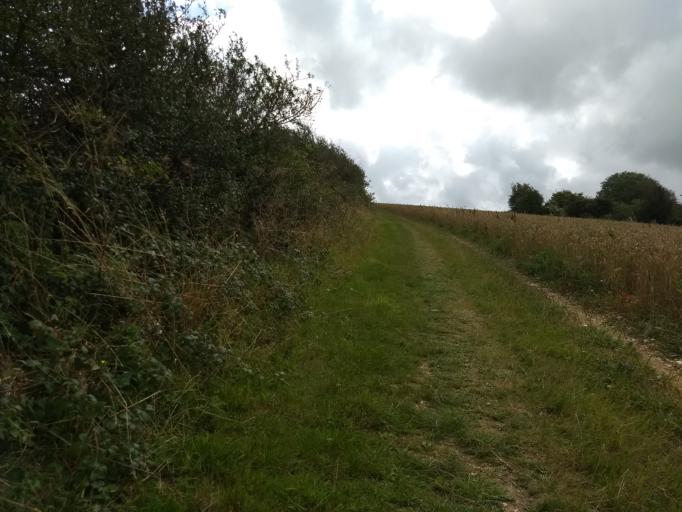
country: GB
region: England
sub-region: Isle of Wight
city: Newport
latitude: 50.6873
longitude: -1.3422
